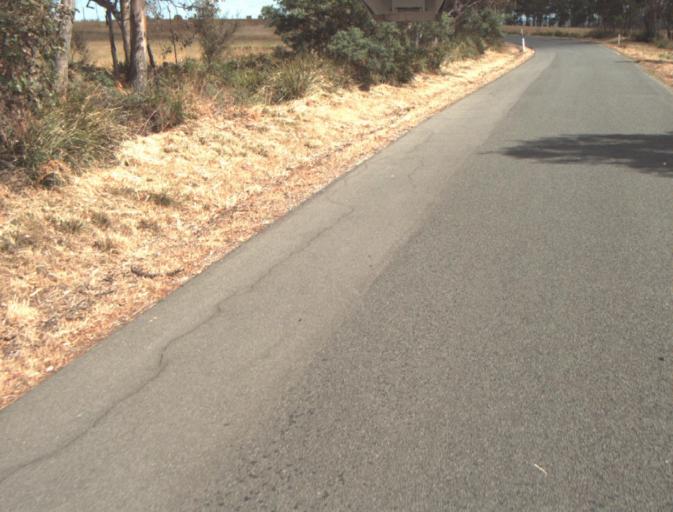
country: AU
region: Tasmania
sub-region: Launceston
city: Mayfield
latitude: -41.2044
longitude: 147.0950
